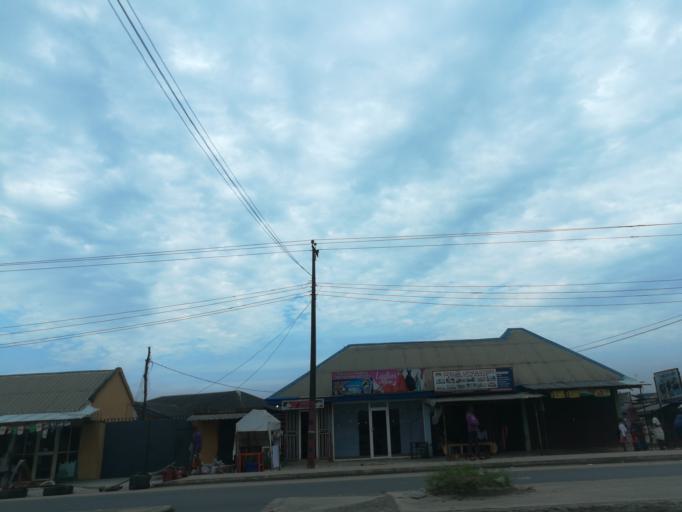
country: NG
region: Rivers
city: Port Harcourt
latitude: 4.8128
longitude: 6.9449
